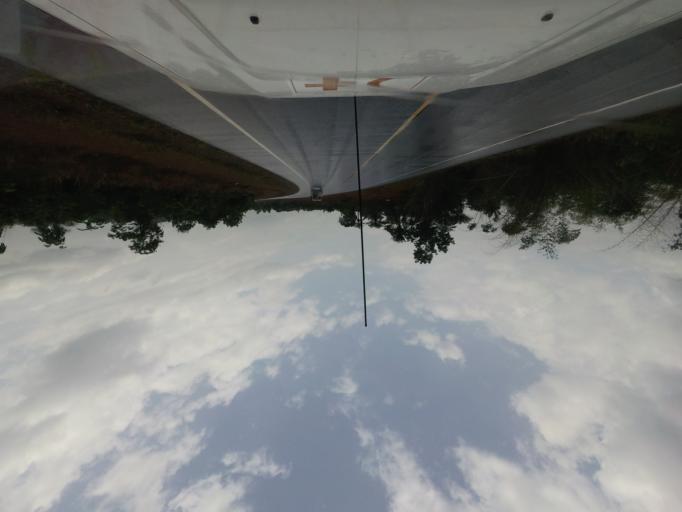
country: LR
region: Montserrado
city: Bensonville City
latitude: 6.3983
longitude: -10.5307
